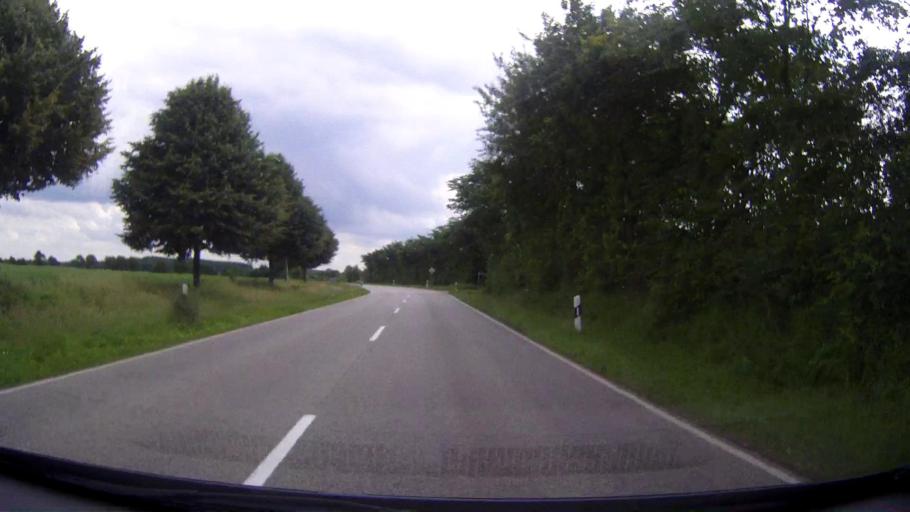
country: DE
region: Schleswig-Holstein
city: Seefeld
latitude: 54.0975
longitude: 9.4679
